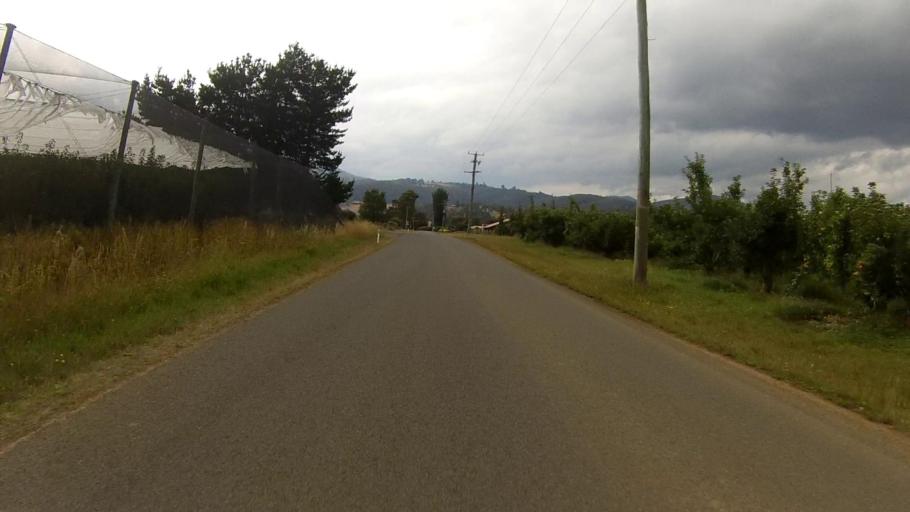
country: AU
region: Tasmania
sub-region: Huon Valley
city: Huonville
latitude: -42.9898
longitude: 147.0616
